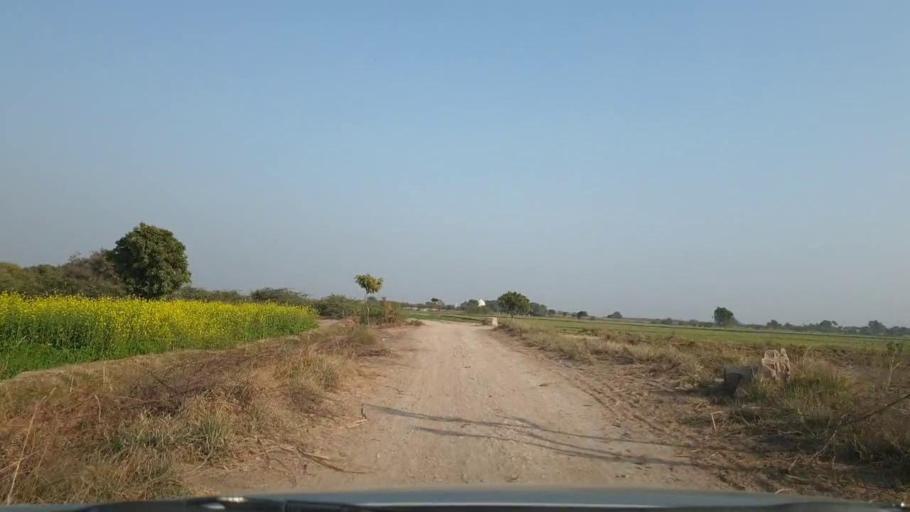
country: PK
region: Sindh
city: Tando Adam
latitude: 25.6706
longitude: 68.6427
